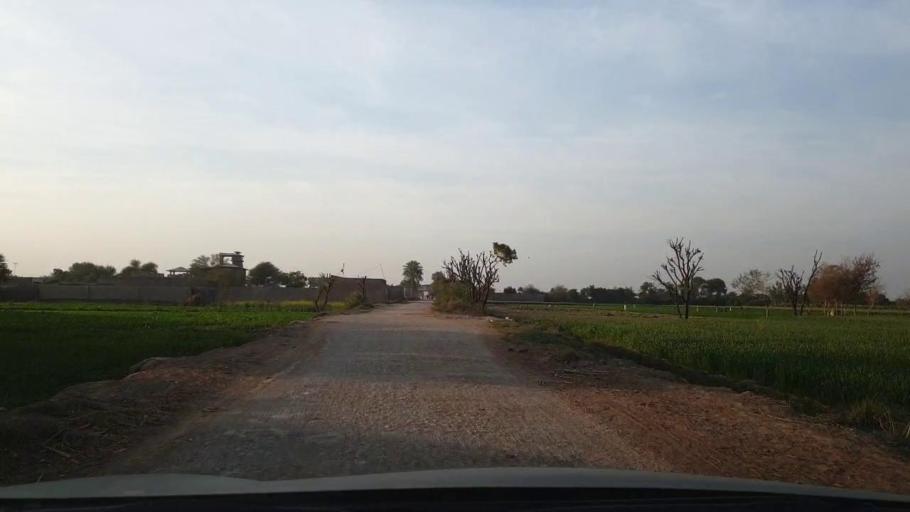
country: PK
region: Sindh
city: Tando Adam
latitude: 25.7105
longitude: 68.7248
